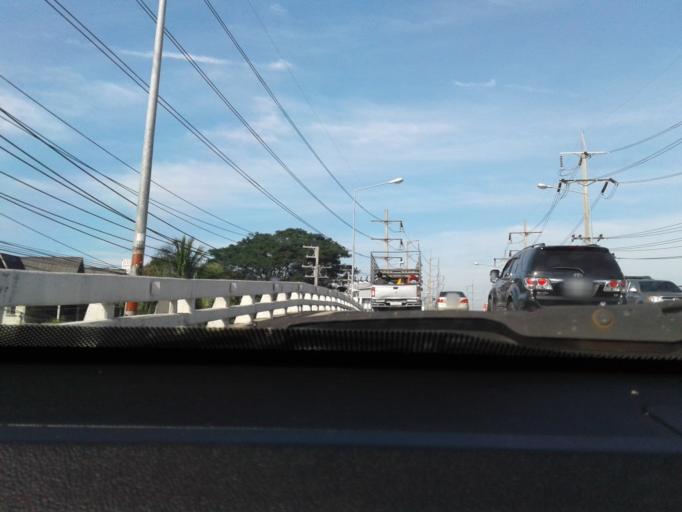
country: TH
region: Nakhon Pathom
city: Salaya
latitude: 13.8042
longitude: 100.3212
